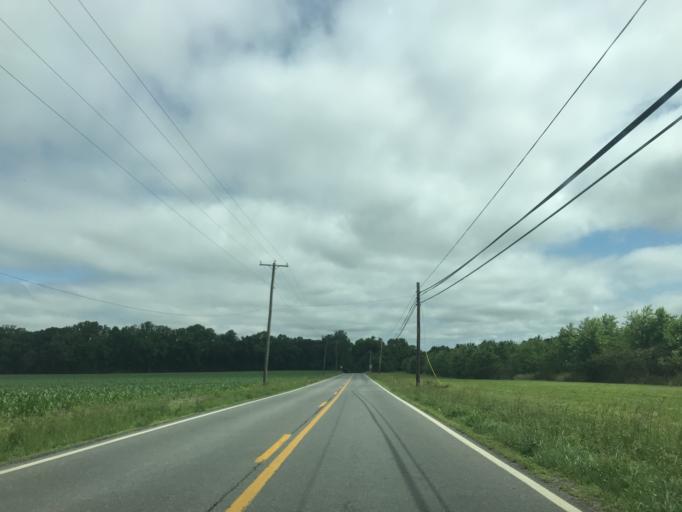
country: US
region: Maryland
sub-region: Caroline County
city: Ridgely
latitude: 38.9120
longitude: -75.9562
